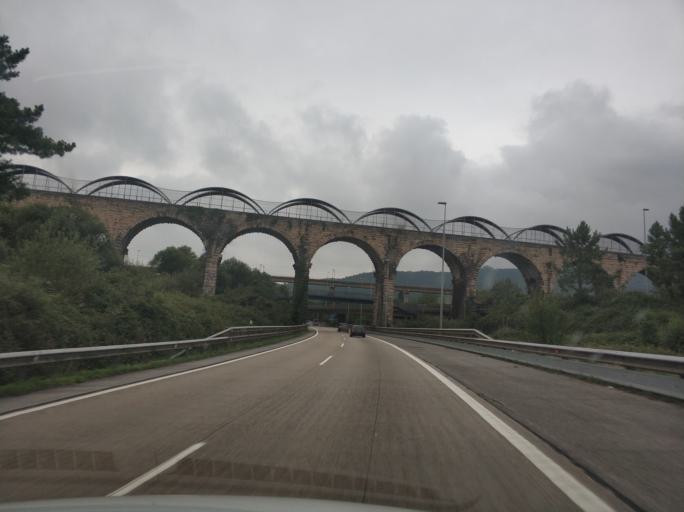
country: ES
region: Asturias
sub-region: Province of Asturias
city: Corvera de Asturias
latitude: 43.5007
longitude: -5.7866
